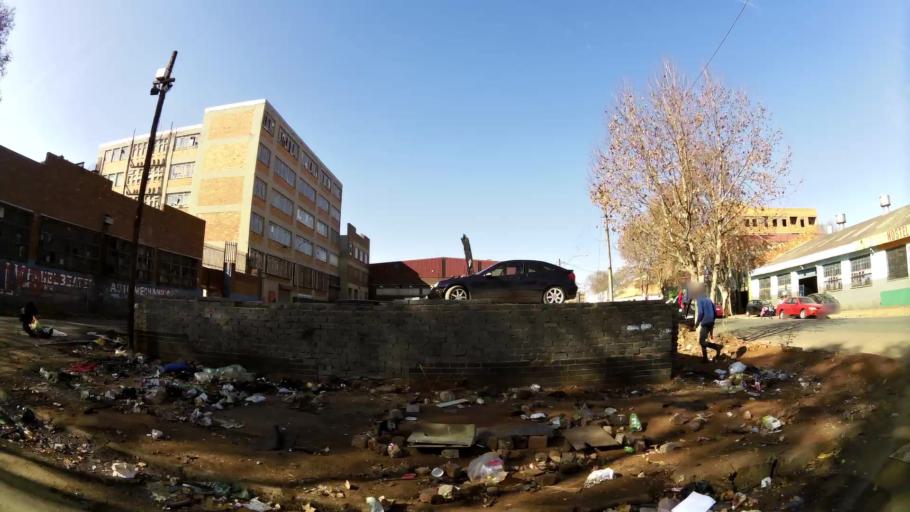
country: ZA
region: Gauteng
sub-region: City of Johannesburg Metropolitan Municipality
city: Johannesburg
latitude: -26.2076
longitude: 28.0669
